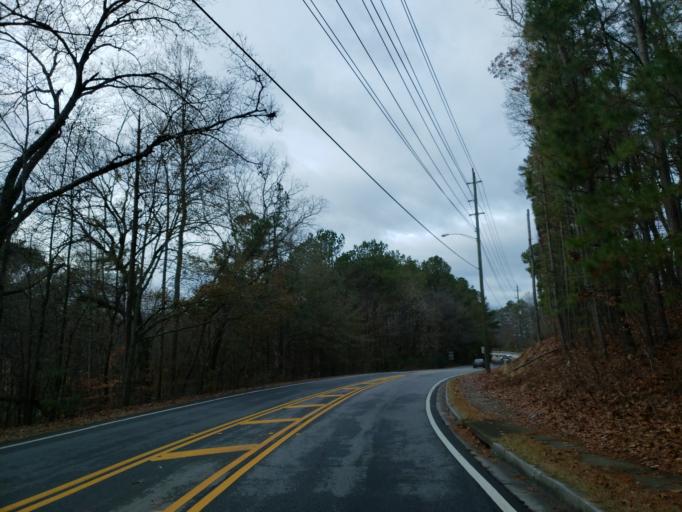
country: US
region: Georgia
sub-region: Cobb County
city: Fair Oaks
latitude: 33.8848
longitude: -84.5933
